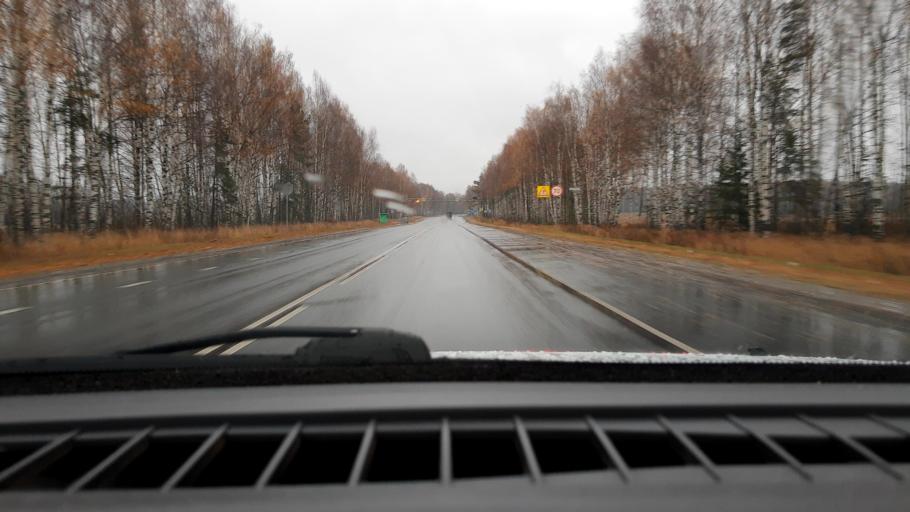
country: RU
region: Nizjnij Novgorod
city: Linda
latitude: 56.6520
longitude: 44.1178
